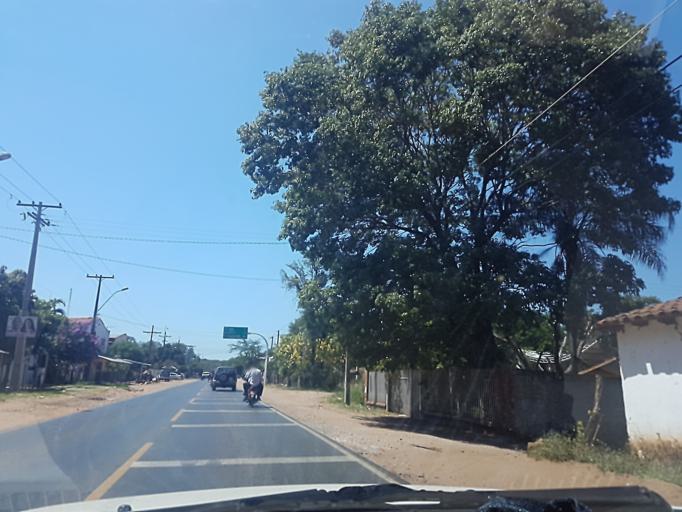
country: PY
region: Central
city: Limpio
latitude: -25.1890
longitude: -57.4644
